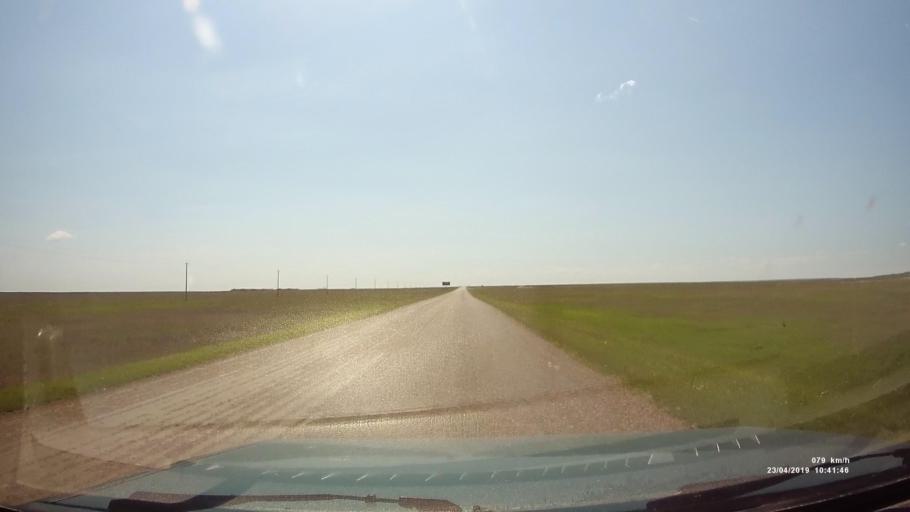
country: RU
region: Kalmykiya
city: Yashalta
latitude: 46.4903
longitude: 42.6391
